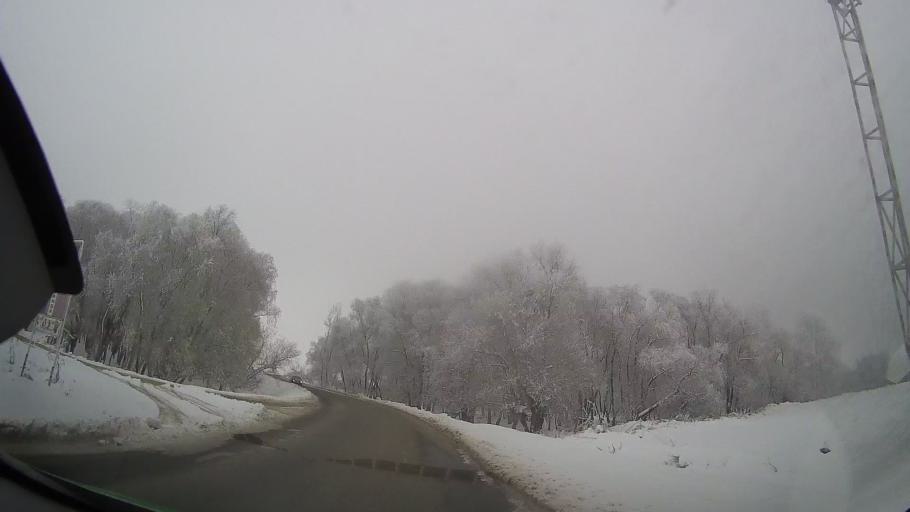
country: RO
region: Neamt
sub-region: Comuna Horia
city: Cotu Vames
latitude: 46.8806
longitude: 26.9732
